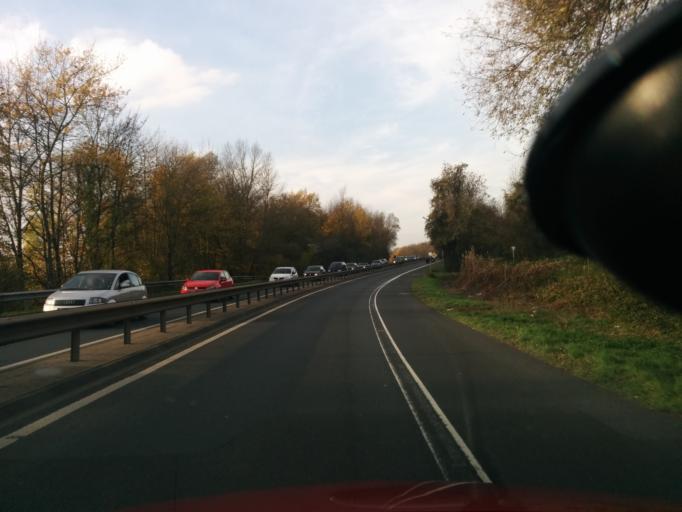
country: DE
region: Rheinland-Pfalz
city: Weitersburg
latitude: 50.4072
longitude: 7.5943
